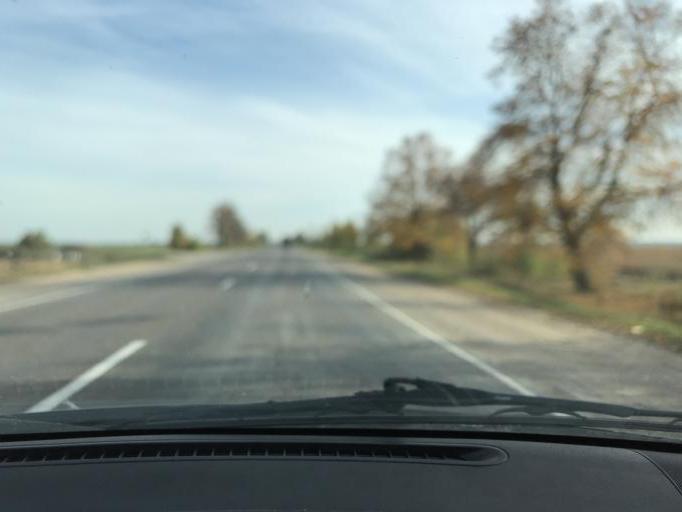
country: BY
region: Brest
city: Asnyezhytsy
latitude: 52.2136
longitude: 26.0433
